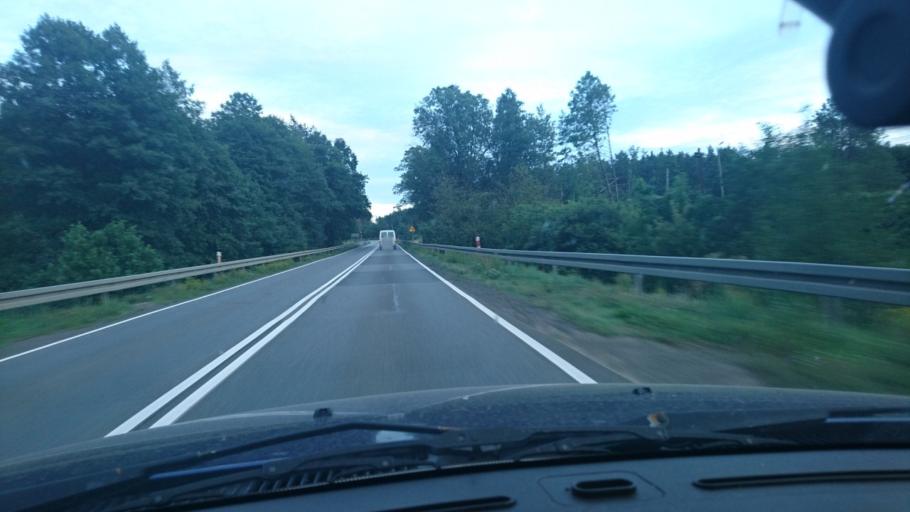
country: PL
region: Silesian Voivodeship
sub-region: Powiat tarnogorski
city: Tworog
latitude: 50.5256
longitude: 18.7193
